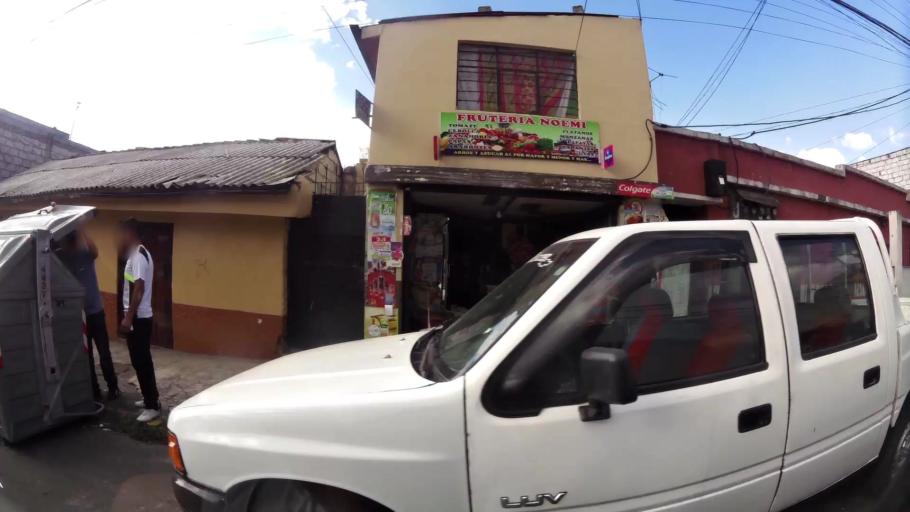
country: EC
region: Pichincha
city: Quito
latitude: -0.1161
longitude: -78.4882
